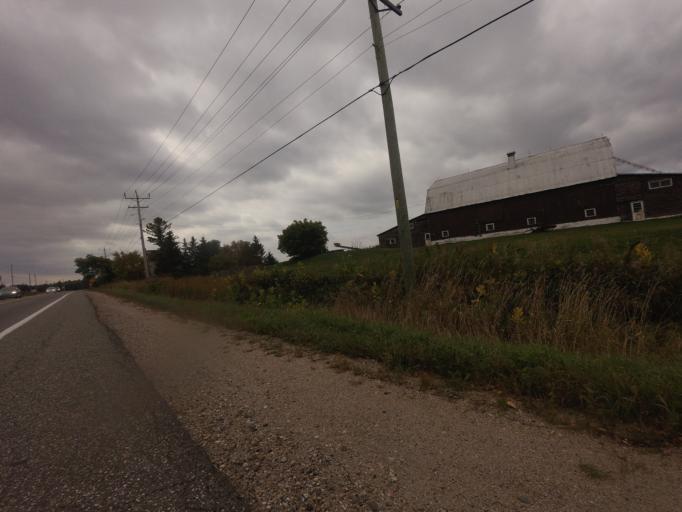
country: CA
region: Quebec
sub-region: Outaouais
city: Wakefield
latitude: 45.9143
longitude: -76.0170
